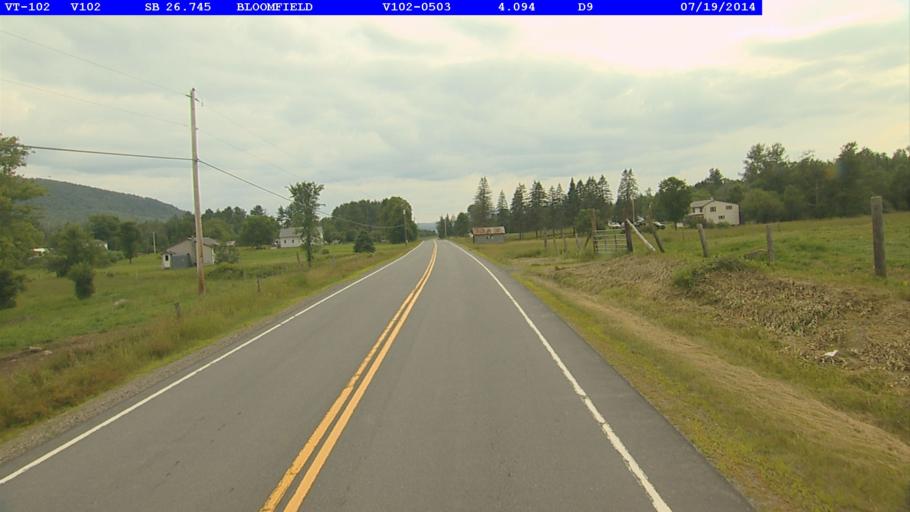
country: US
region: New Hampshire
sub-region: Coos County
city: Colebrook
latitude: 44.7905
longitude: -71.5790
